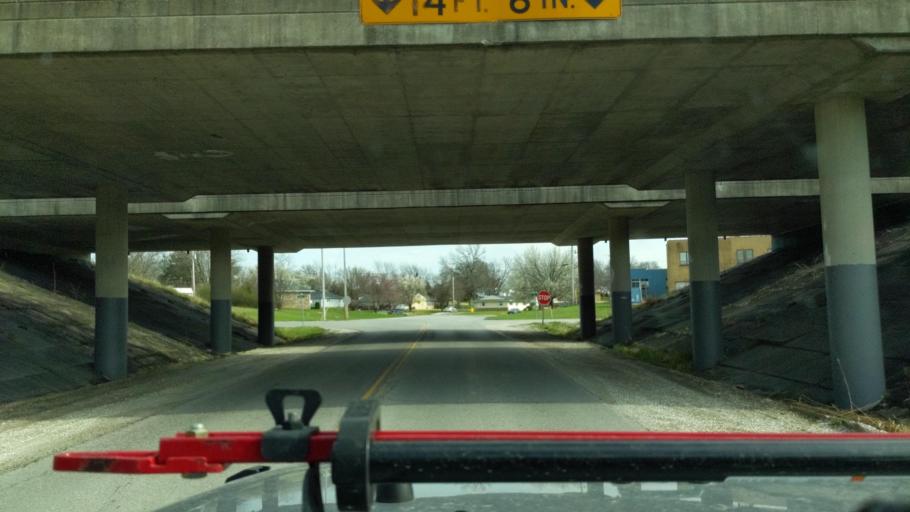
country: US
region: Missouri
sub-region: Macon County
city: Macon
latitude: 39.7522
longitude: -92.4741
